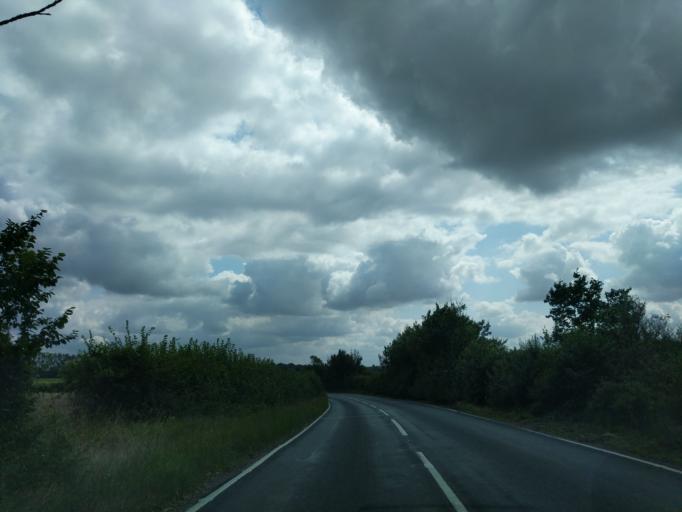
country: GB
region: England
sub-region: Cambridgeshire
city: Isleham
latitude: 52.3069
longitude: 0.4224
